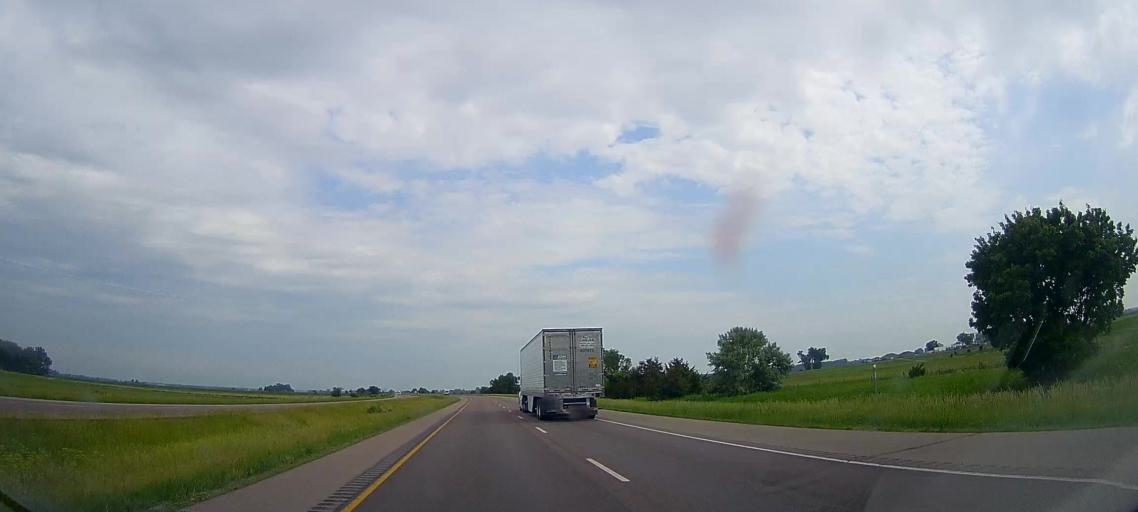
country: US
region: Iowa
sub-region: Monona County
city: Onawa
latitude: 42.0780
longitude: -96.1741
